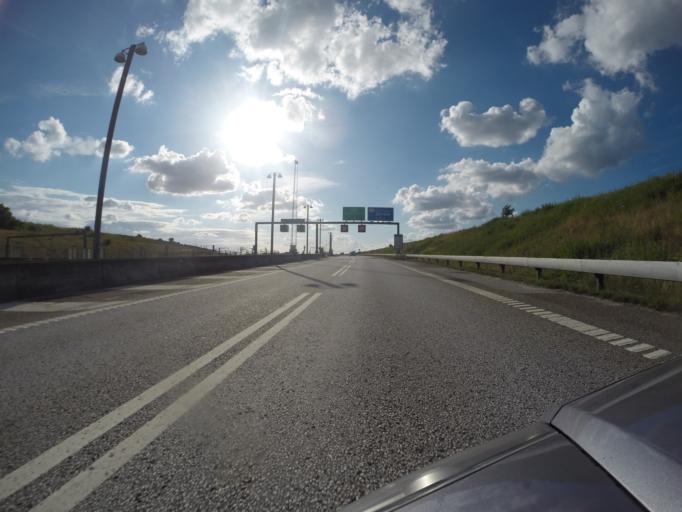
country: DK
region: Capital Region
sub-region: Dragor Kommune
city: Dragor
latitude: 55.6318
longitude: 12.6757
